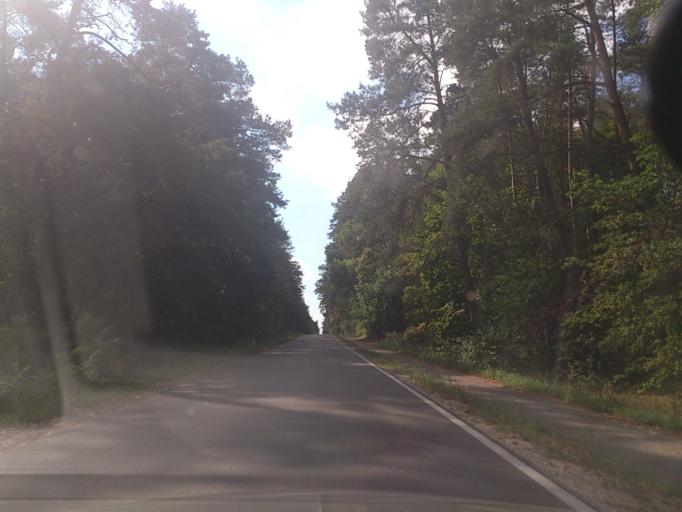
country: PL
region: Kujawsko-Pomorskie
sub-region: Powiat golubsko-dobrzynski
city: Golub-Dobrzyn
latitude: 53.0905
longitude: 19.0366
